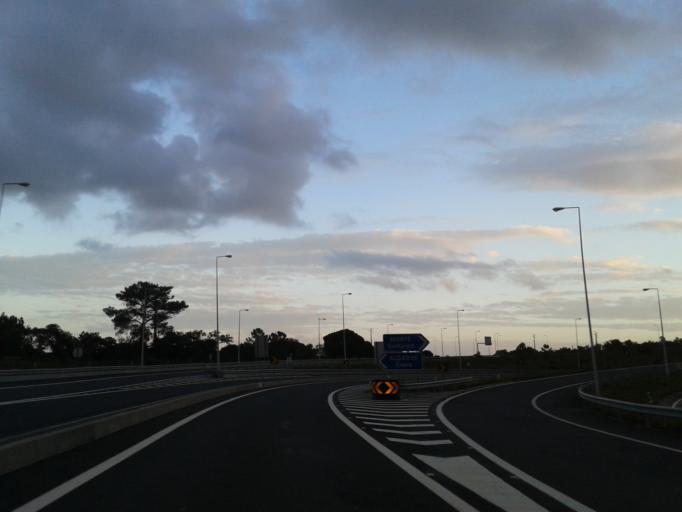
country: PT
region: Santarem
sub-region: Benavente
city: Poceirao
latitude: 38.8394
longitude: -8.7264
